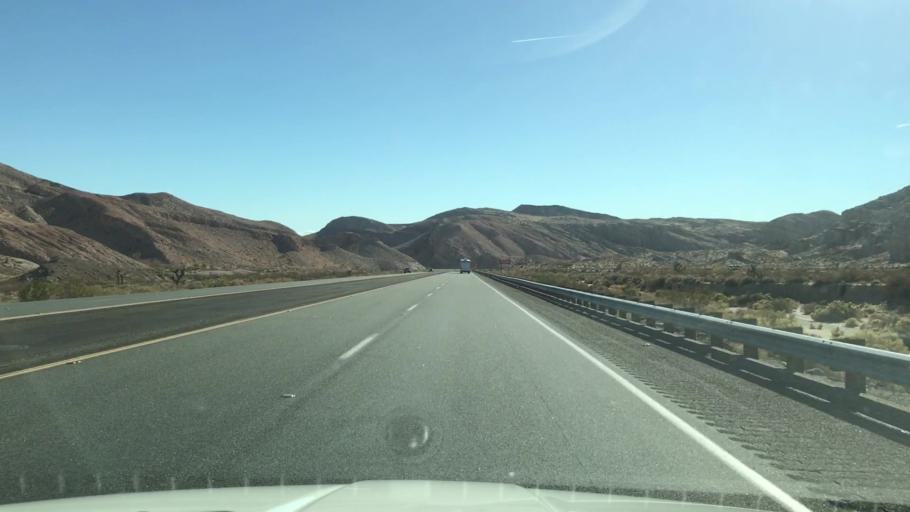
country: US
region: California
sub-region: Kern County
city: California City
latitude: 35.3711
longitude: -117.9816
